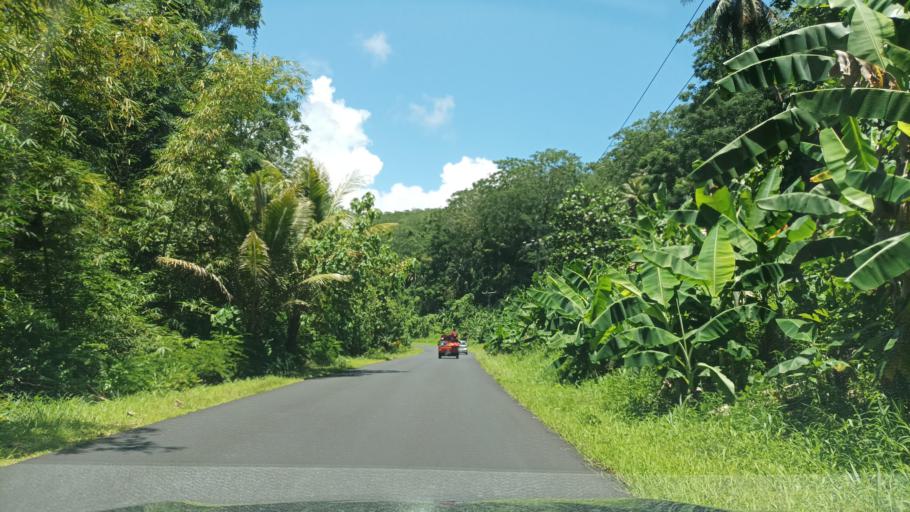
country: FM
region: Pohnpei
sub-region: Madolenihm Municipality
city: Madolenihm Municipality Government
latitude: 6.9175
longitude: 158.3223
